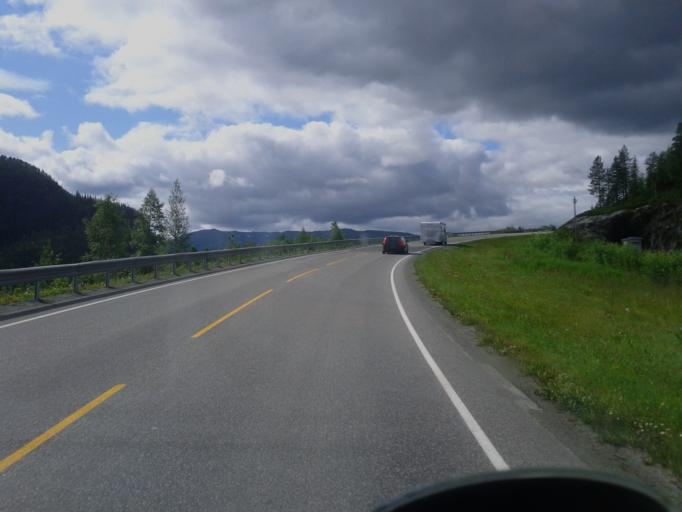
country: NO
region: Nord-Trondelag
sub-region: Grong
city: Grong
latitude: 64.5373
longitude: 12.4448
